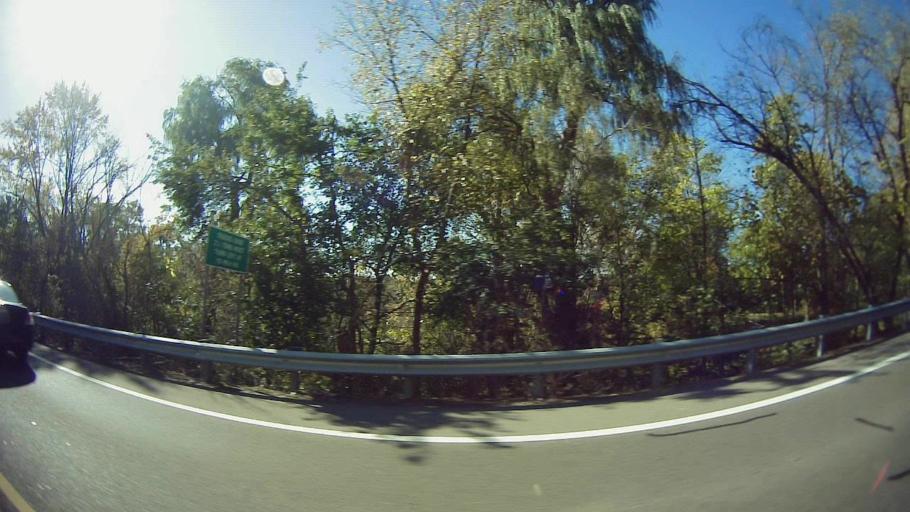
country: US
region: Michigan
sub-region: Oakland County
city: Farmington
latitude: 42.4711
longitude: -83.3754
